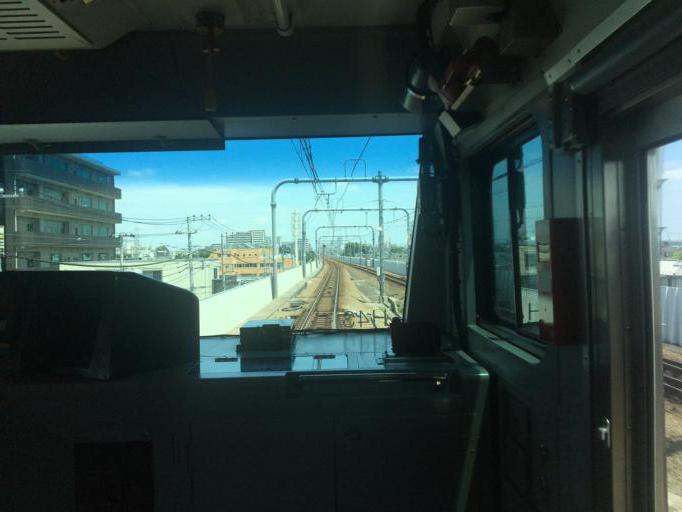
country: JP
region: Tokyo
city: Nishi-Tokyo-shi
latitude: 35.7013
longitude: 139.5159
